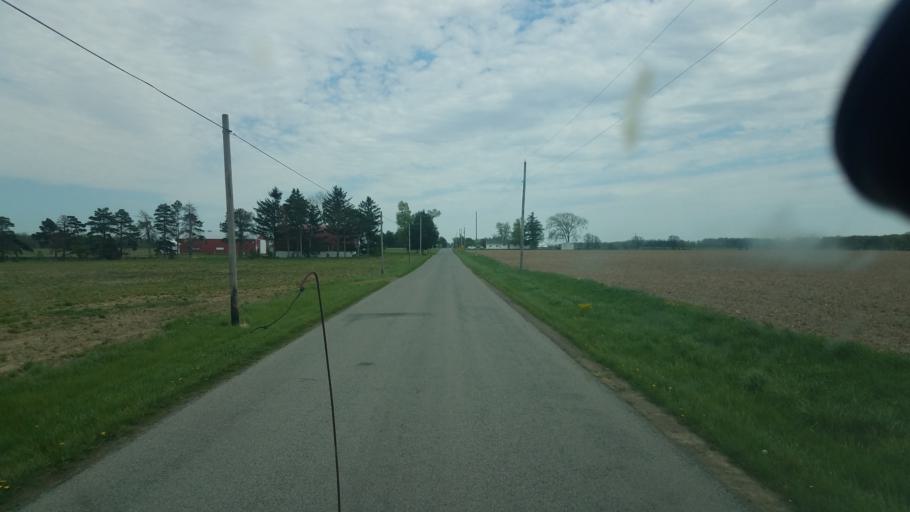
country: US
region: Ohio
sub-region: Allen County
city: Bluffton
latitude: 40.8119
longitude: -83.9418
